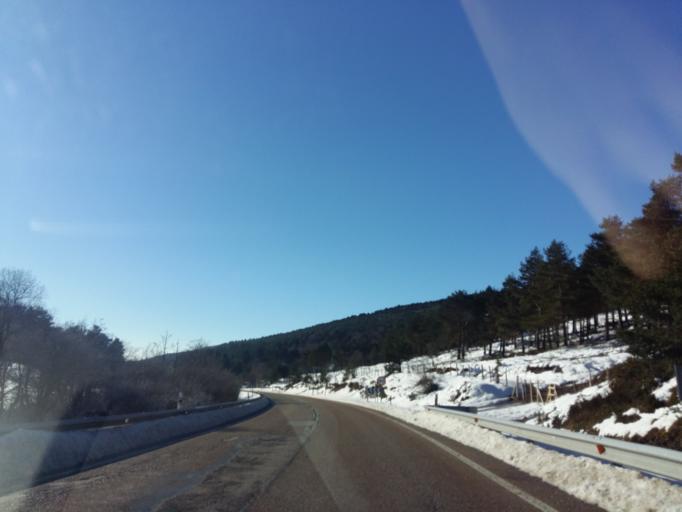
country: ES
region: Basque Country
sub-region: Bizkaia
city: Lanestosa
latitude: 43.1338
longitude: -3.4555
